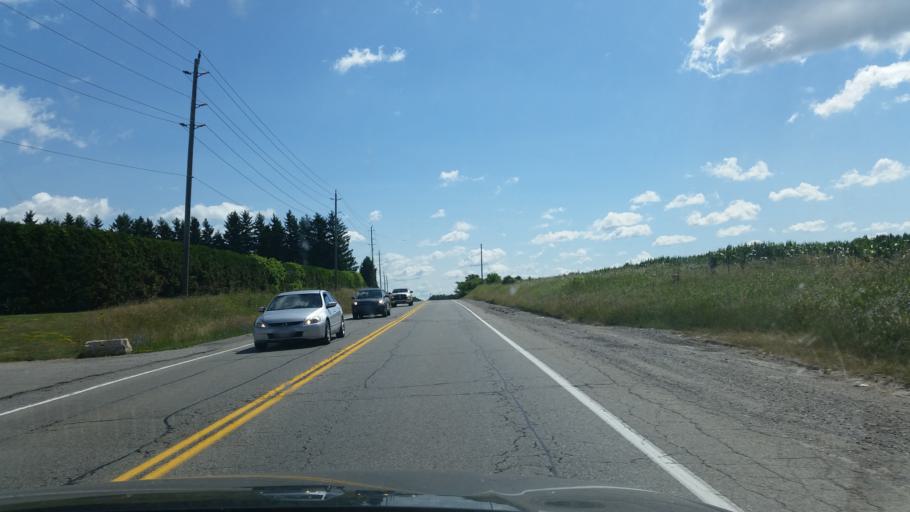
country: CA
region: Ontario
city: Vaughan
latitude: 43.9104
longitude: -79.6133
